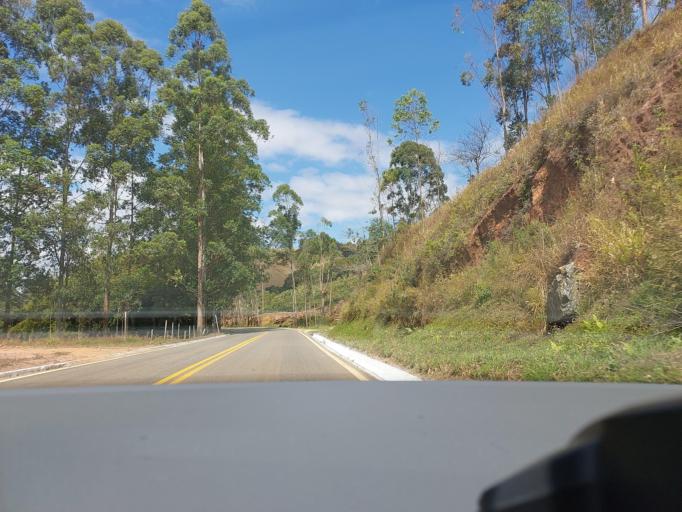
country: BR
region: Minas Gerais
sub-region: Visconde Do Rio Branco
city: Visconde do Rio Branco
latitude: -20.9189
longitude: -42.6385
